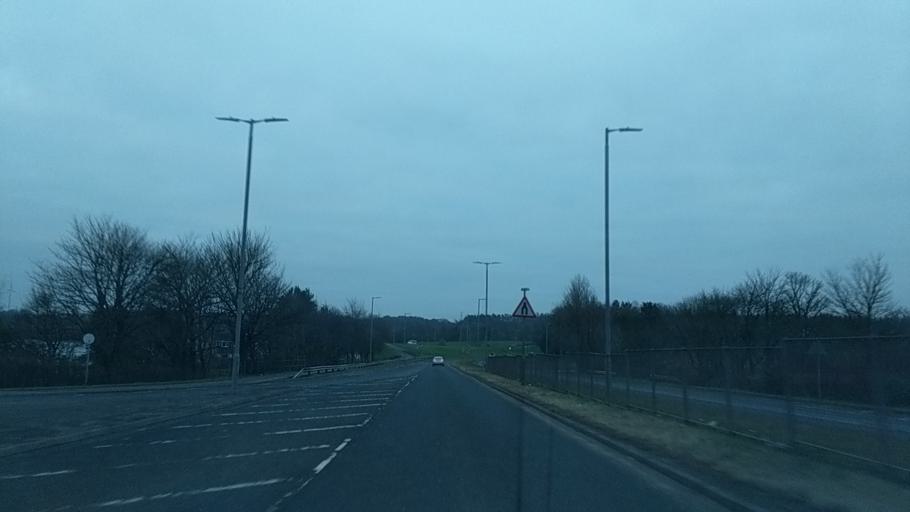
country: GB
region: Scotland
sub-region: South Lanarkshire
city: East Kilbride
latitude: 55.7538
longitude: -4.1569
